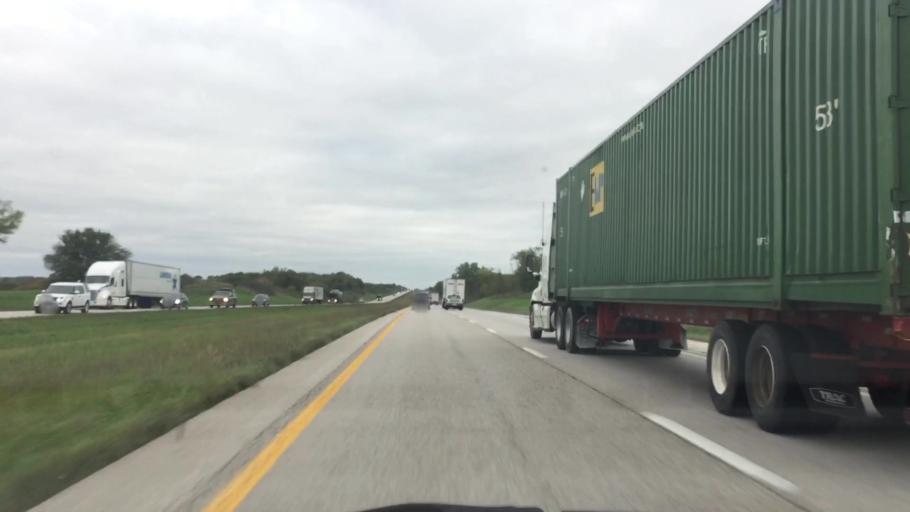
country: US
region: Missouri
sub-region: Clinton County
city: Cameron
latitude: 39.6938
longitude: -94.2290
